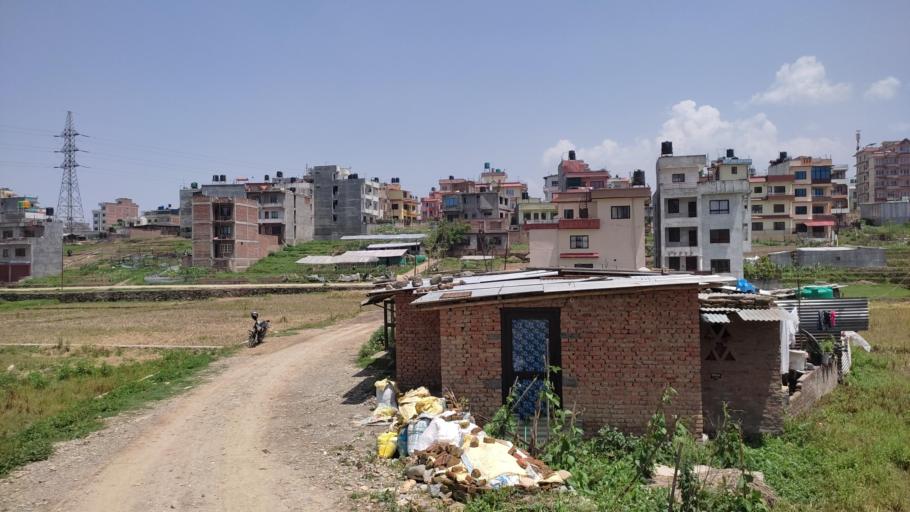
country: NP
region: Central Region
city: Kirtipur
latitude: 27.6689
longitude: 85.2656
